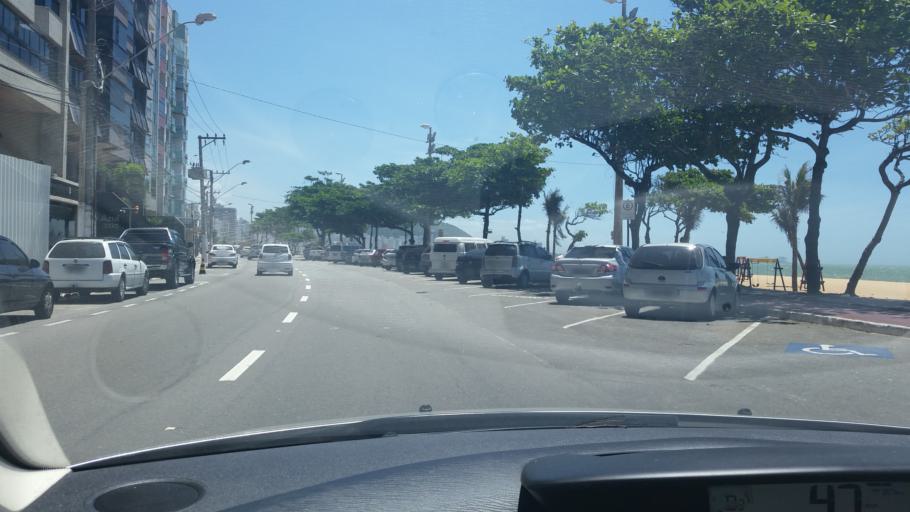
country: BR
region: Espirito Santo
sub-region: Vila Velha
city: Vila Velha
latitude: -20.3519
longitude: -40.2839
